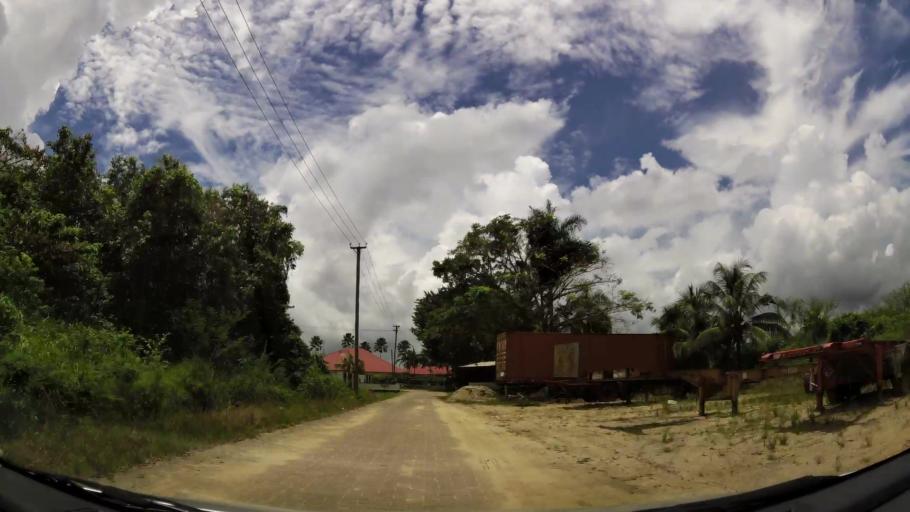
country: SR
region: Paramaribo
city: Paramaribo
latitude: 5.8071
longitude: -55.2421
